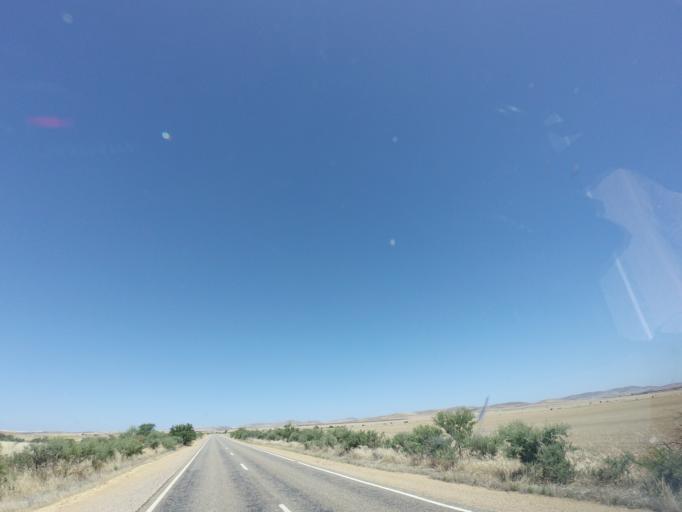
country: AU
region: South Australia
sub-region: Peterborough
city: Peterborough
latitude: -32.7121
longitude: 138.4453
